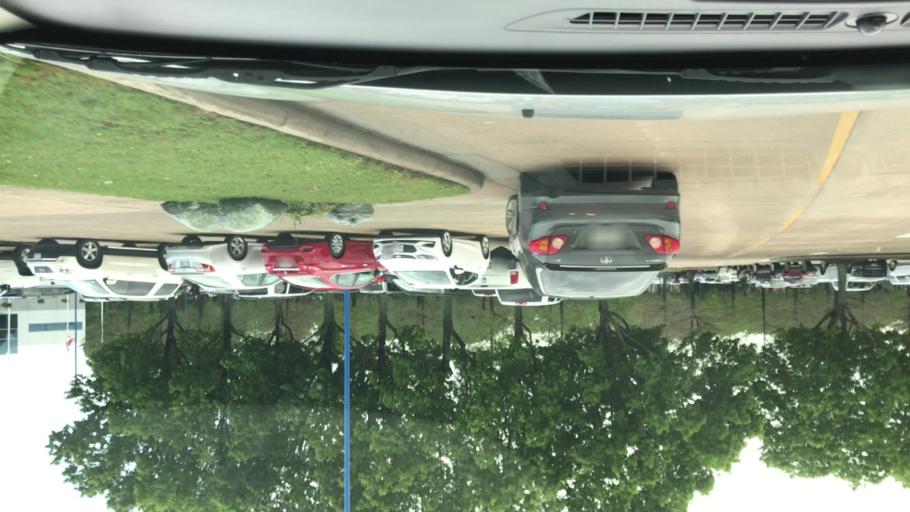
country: US
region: Texas
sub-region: Harris County
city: Nassau Bay
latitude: 29.5518
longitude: -95.0964
